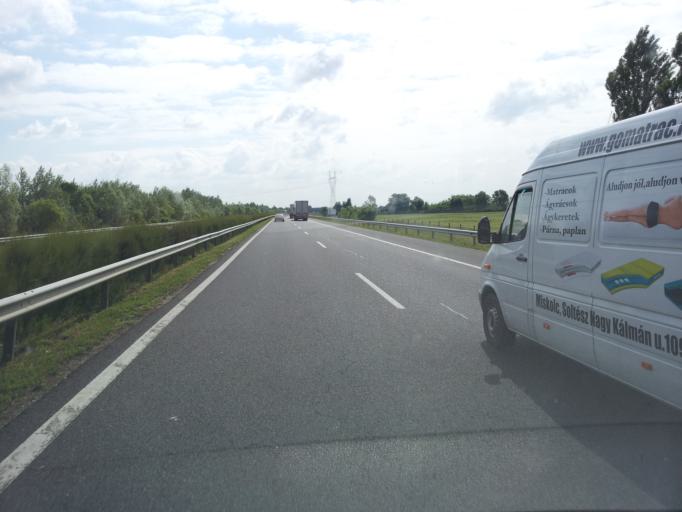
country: HU
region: Borsod-Abauj-Zemplen
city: Hejobaba
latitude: 47.8739
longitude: 20.9465
